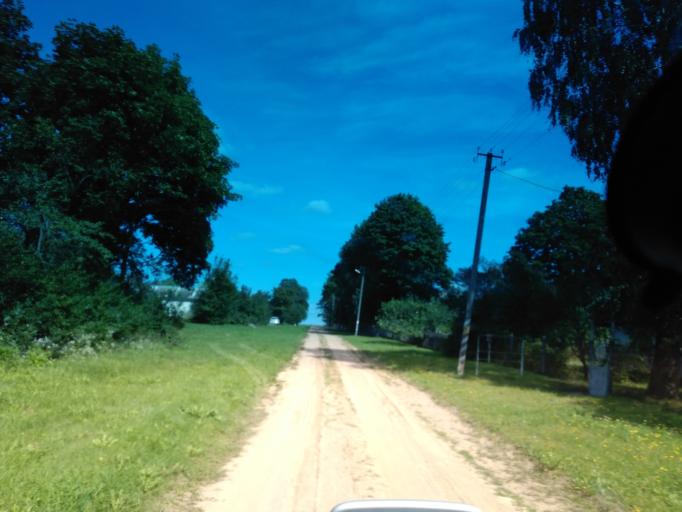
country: BY
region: Minsk
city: Stan'kava
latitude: 53.6397
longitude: 27.3131
